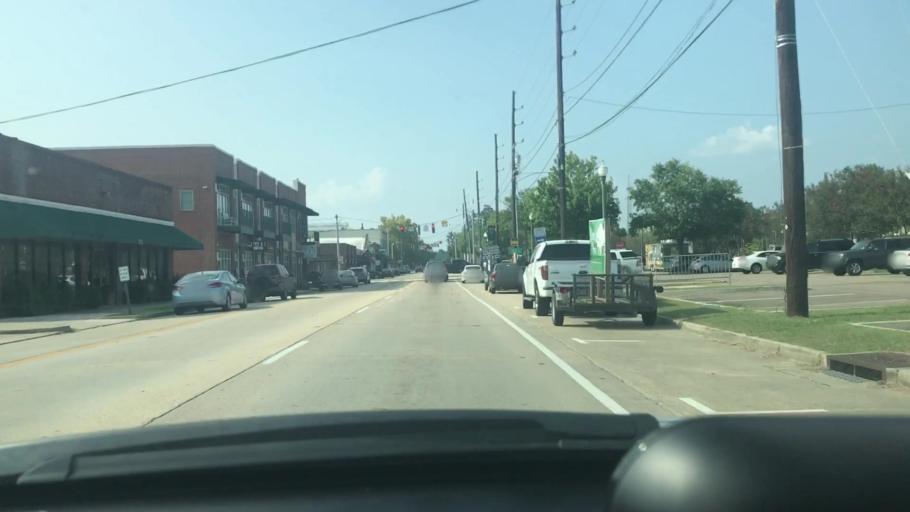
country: US
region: Louisiana
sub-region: Tangipahoa Parish
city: Hammond
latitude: 30.5022
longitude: -90.4608
